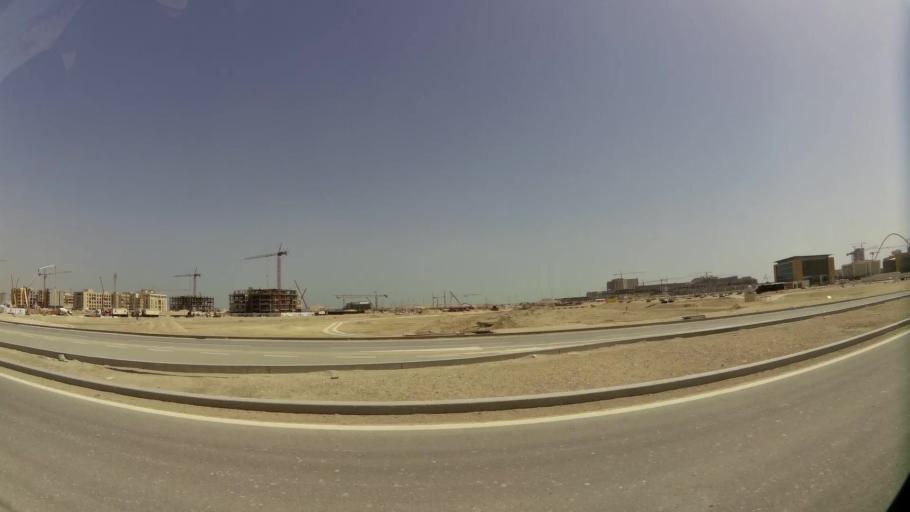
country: QA
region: Baladiyat Umm Salal
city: Umm Salal Muhammad
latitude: 25.4051
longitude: 51.5067
